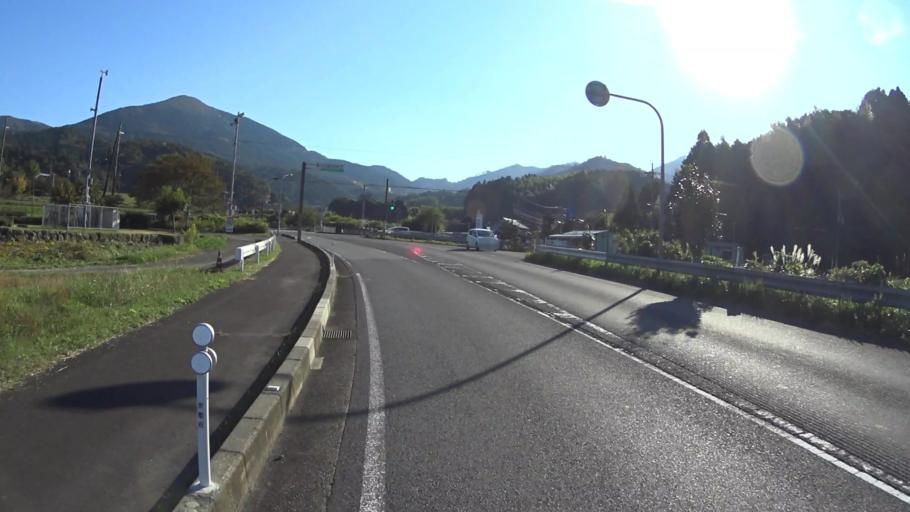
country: JP
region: Kyoto
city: Miyazu
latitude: 35.4692
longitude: 135.0849
